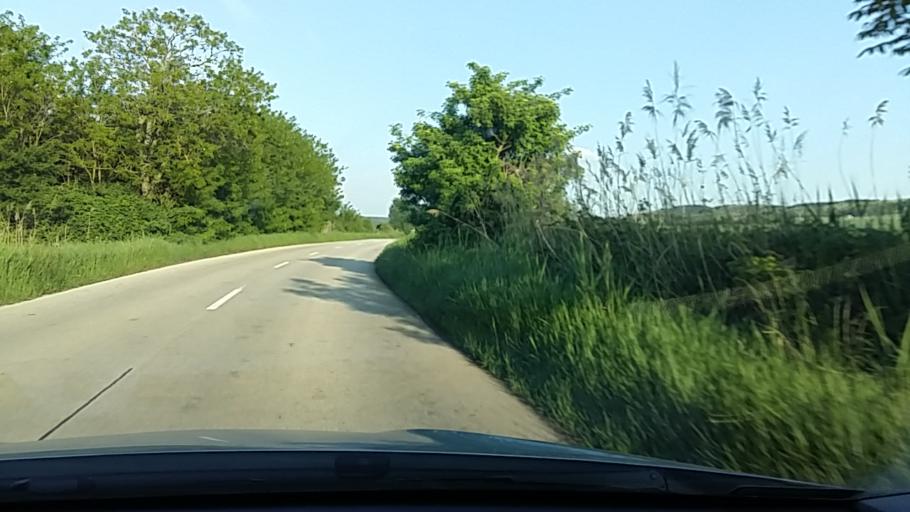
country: HU
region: Pest
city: Szod
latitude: 47.7557
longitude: 19.1949
